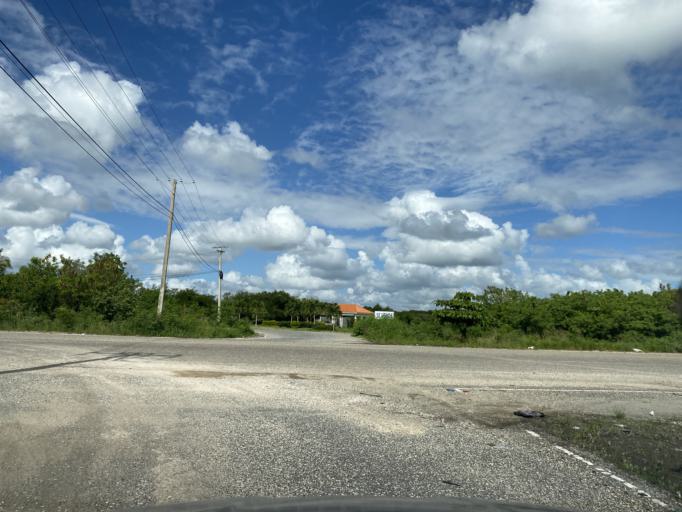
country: DO
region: Santo Domingo
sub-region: Santo Domingo
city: Boca Chica
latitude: 18.4516
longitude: -69.5940
